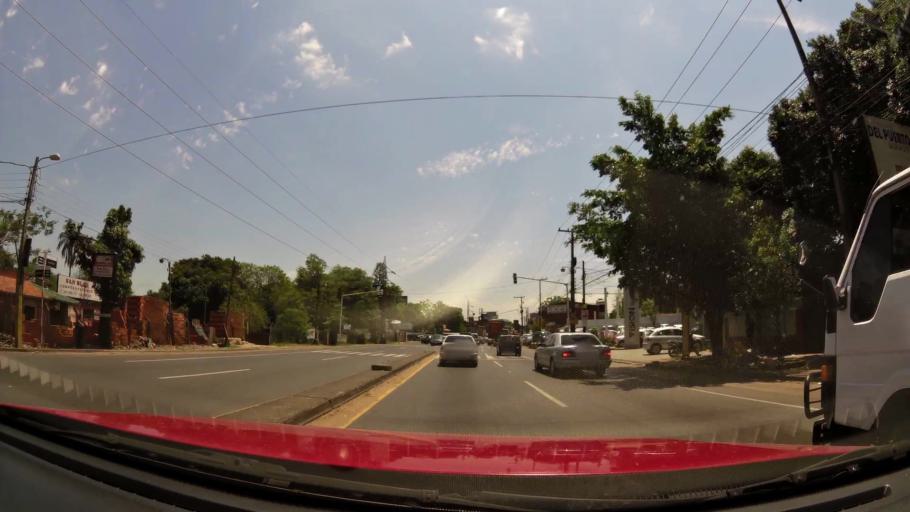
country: PY
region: Central
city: Villa Elisa
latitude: -25.3453
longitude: -57.5794
